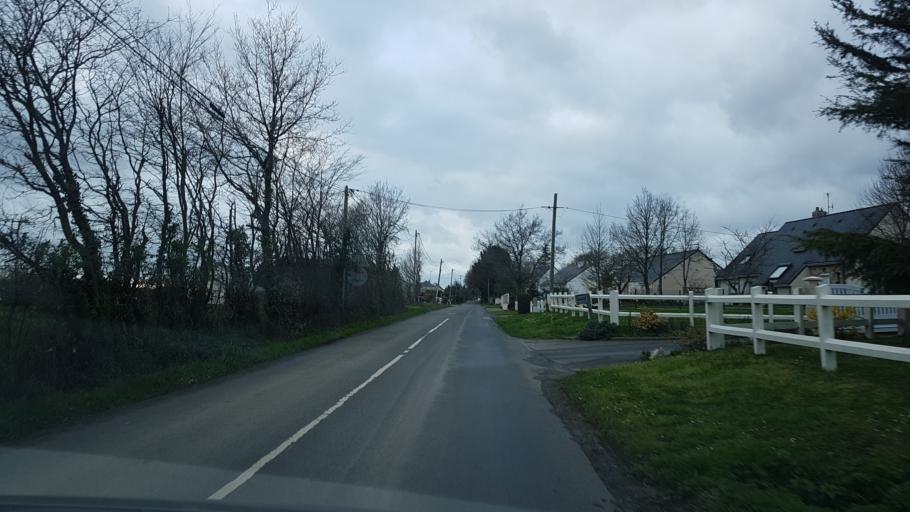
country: FR
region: Pays de la Loire
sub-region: Departement de la Loire-Atlantique
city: Le Gavre
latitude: 47.5229
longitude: -1.7531
